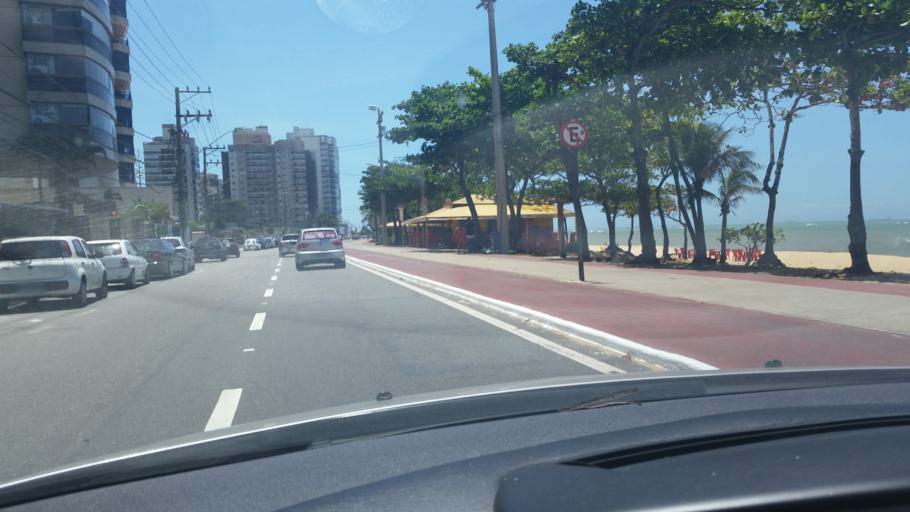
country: BR
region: Espirito Santo
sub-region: Vila Velha
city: Vila Velha
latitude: -20.3581
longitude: -40.2918
